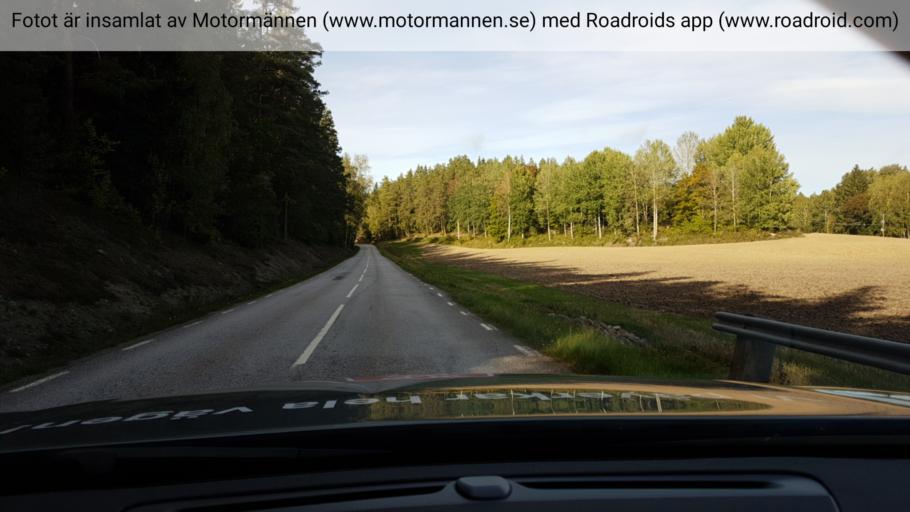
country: SE
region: OEstergoetland
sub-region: Valdemarsviks Kommun
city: Valdemarsvik
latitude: 58.1611
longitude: 16.6042
